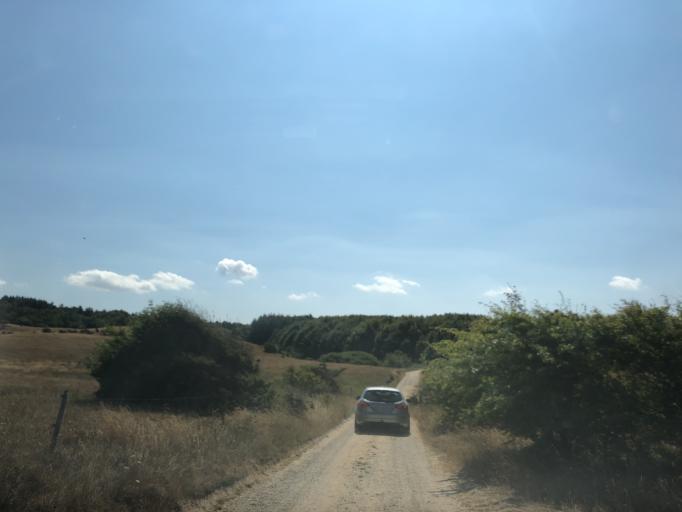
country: DK
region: North Denmark
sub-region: Morso Kommune
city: Nykobing Mors
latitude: 56.8430
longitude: 9.0042
